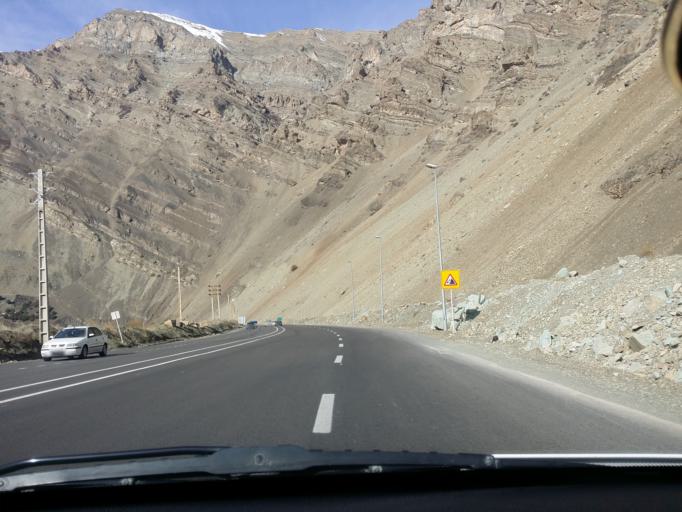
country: IR
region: Alborz
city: Karaj
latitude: 36.0115
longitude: 51.1315
